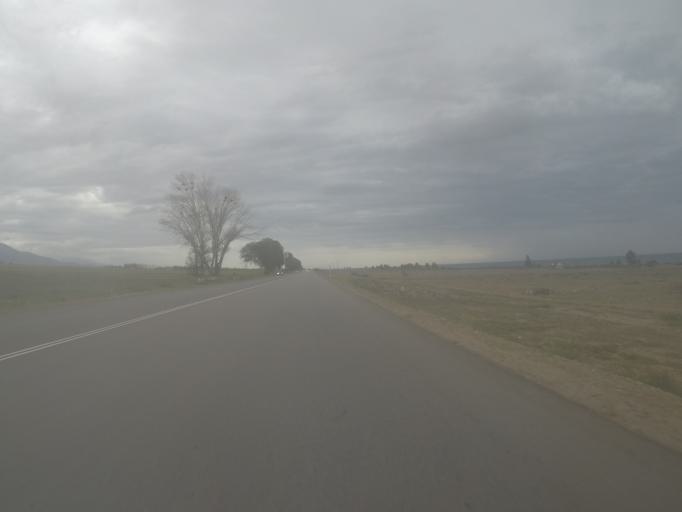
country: KG
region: Ysyk-Koel
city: Cholpon-Ata
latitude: 42.5984
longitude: 76.7980
